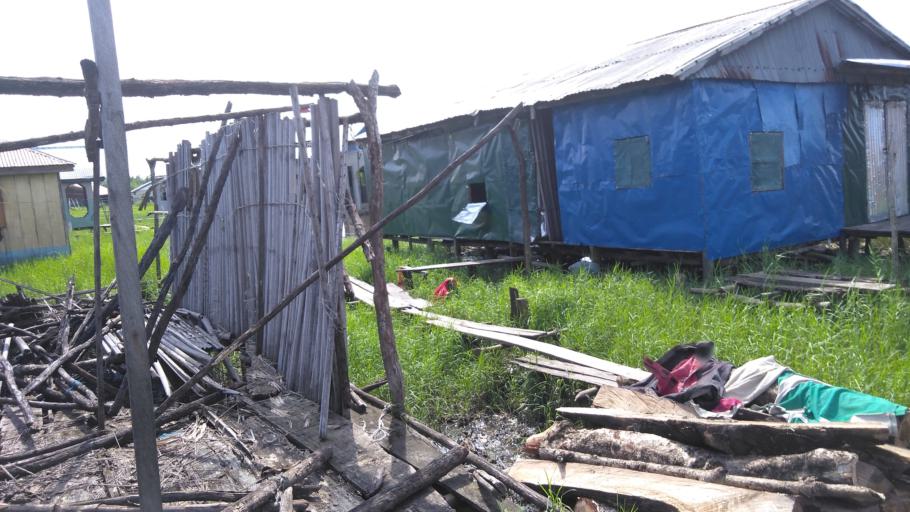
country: NG
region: Ondo
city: Igbekebo
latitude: 5.9220
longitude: 4.9662
